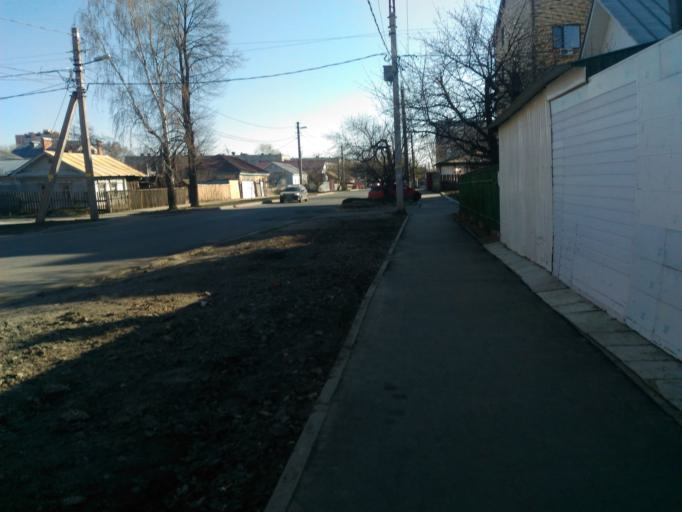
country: RU
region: Ulyanovsk
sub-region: Ulyanovskiy Rayon
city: Ulyanovsk
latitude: 54.3519
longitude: 48.3771
